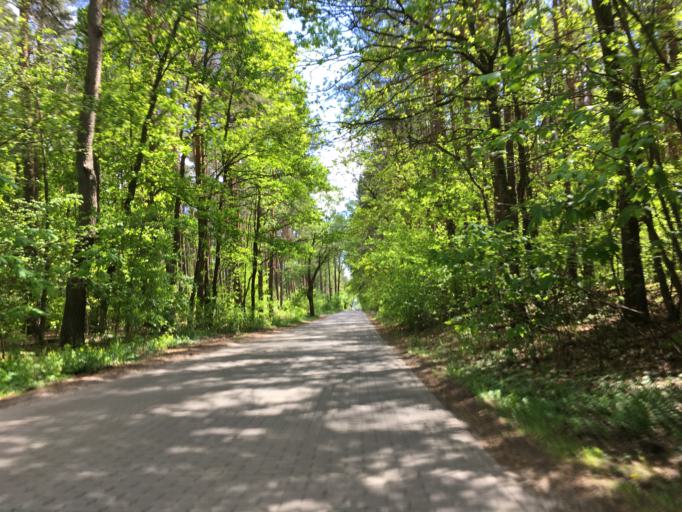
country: DE
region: Brandenburg
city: Biesenthal
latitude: 52.7475
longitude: 13.6502
